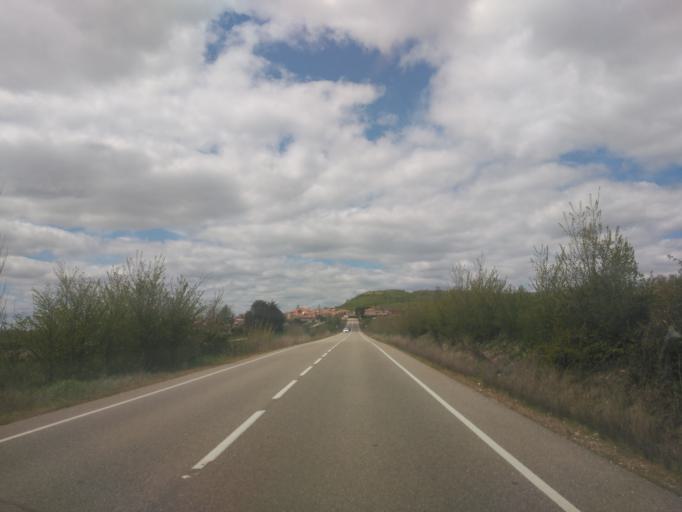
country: ES
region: Castille and Leon
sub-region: Provincia de Salamanca
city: Almenara de Tormes
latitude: 41.0616
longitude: -5.8143
